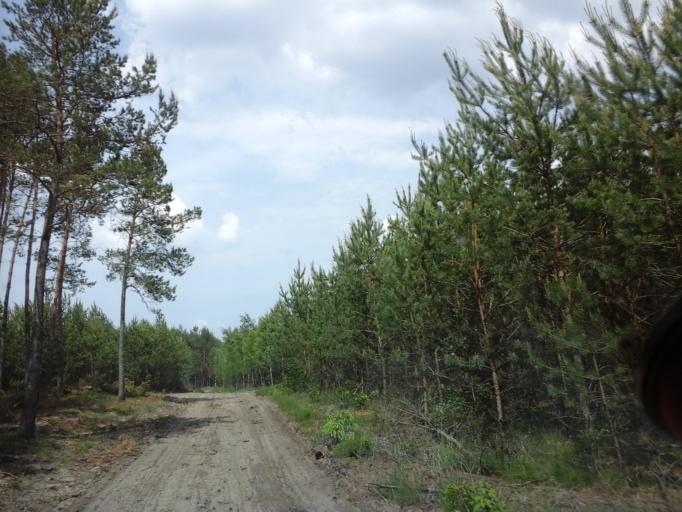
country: PL
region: West Pomeranian Voivodeship
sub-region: Powiat choszczenski
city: Drawno
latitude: 53.1247
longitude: 15.7601
